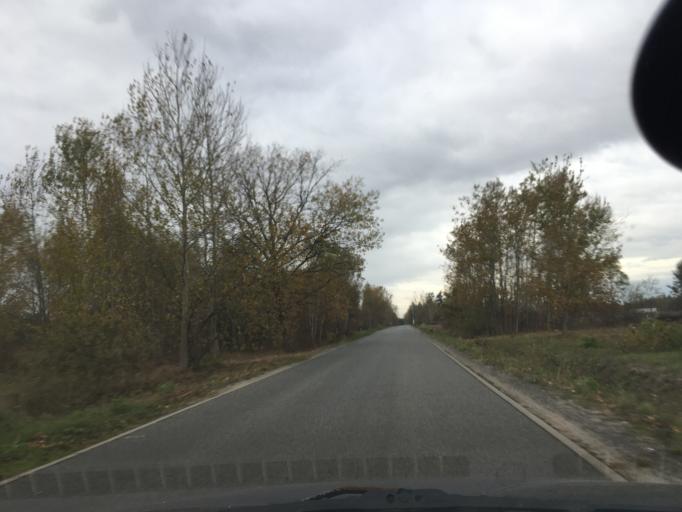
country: PL
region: Lodz Voivodeship
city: Zabia Wola
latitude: 52.0223
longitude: 20.7157
